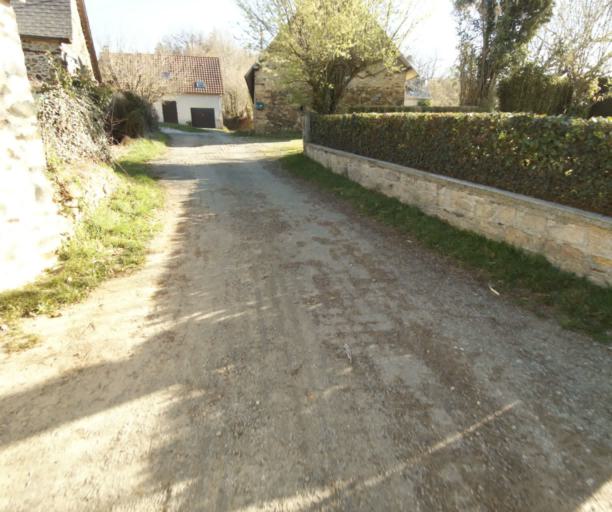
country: FR
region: Limousin
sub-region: Departement de la Correze
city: Seilhac
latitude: 45.3646
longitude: 1.7582
